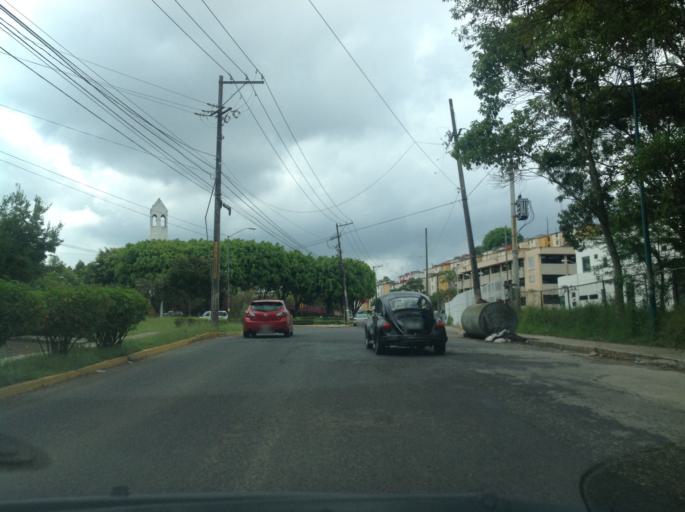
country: MX
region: Veracruz
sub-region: Xalapa
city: Lomas Verdes
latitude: 19.5075
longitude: -96.8996
